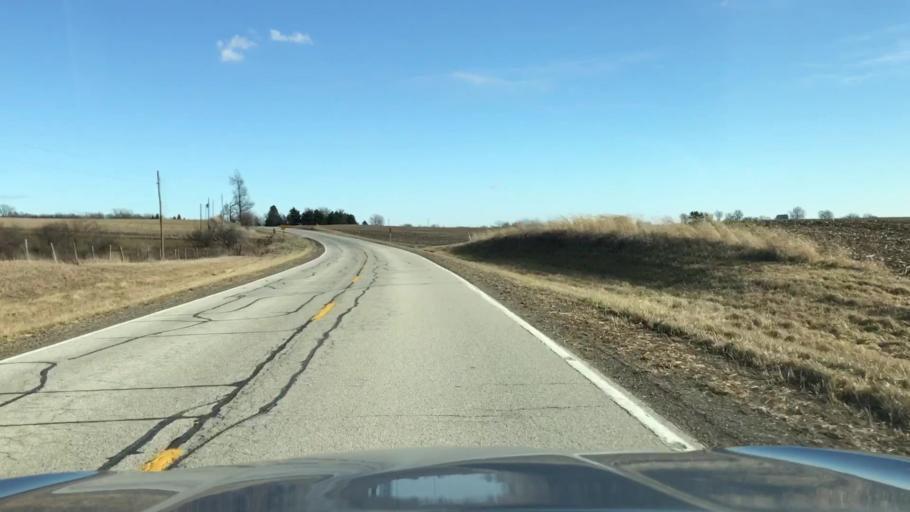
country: US
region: Illinois
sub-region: McLean County
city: Lexington
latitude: 40.6488
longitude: -88.8738
